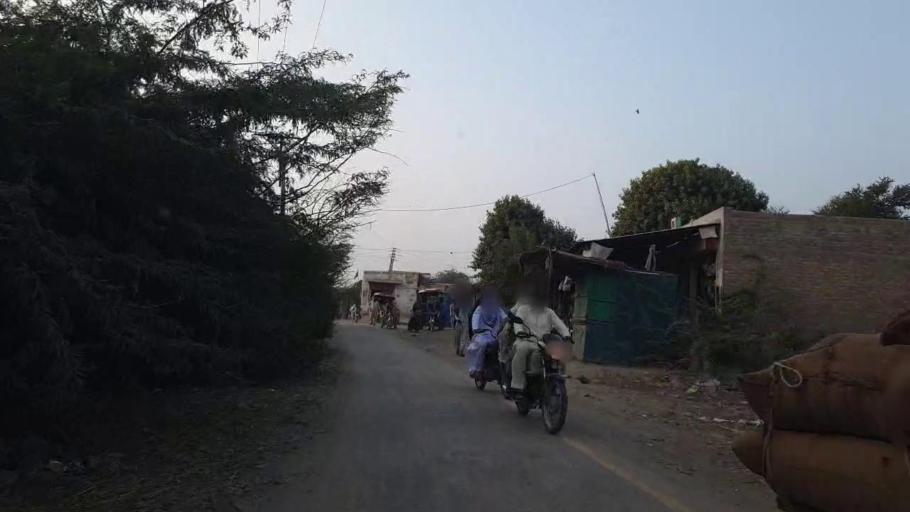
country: PK
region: Sindh
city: Tando Ghulam Ali
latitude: 25.1468
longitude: 68.9550
